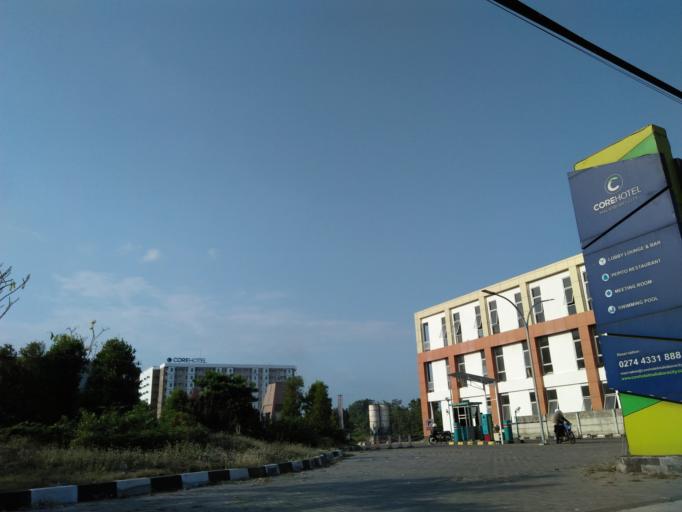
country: ID
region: Daerah Istimewa Yogyakarta
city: Depok
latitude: -7.7832
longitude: 110.4182
